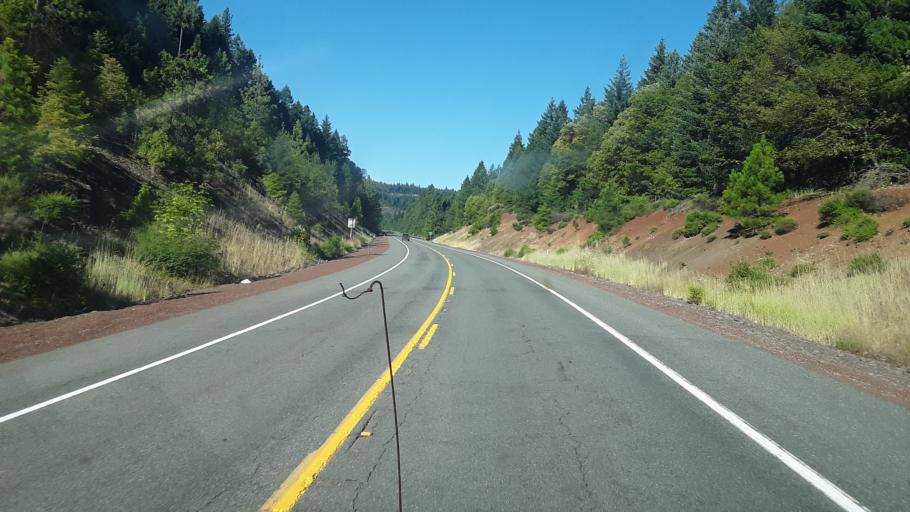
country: US
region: Oregon
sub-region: Jackson County
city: Shady Cove
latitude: 42.6734
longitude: -122.6340
